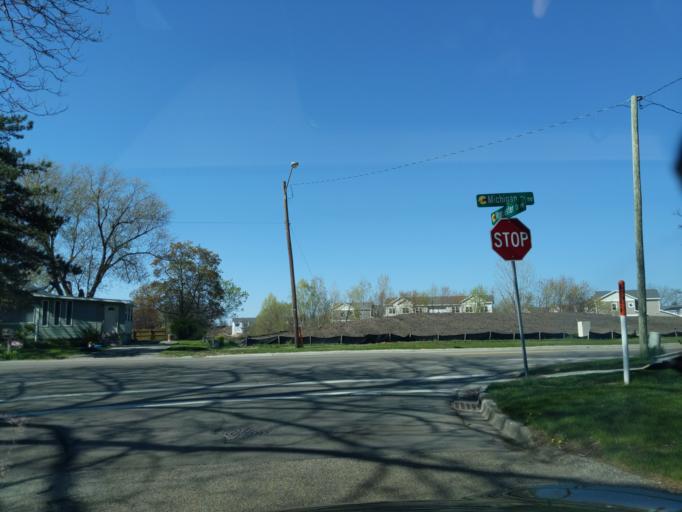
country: US
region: Michigan
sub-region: Kent County
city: East Grand Rapids
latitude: 42.9698
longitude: -85.6153
